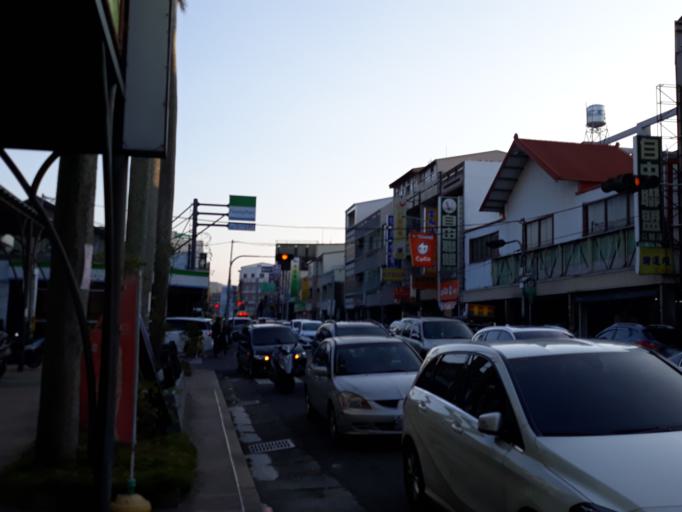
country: TW
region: Taiwan
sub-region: Miaoli
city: Miaoli
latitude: 24.5053
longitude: 120.8271
